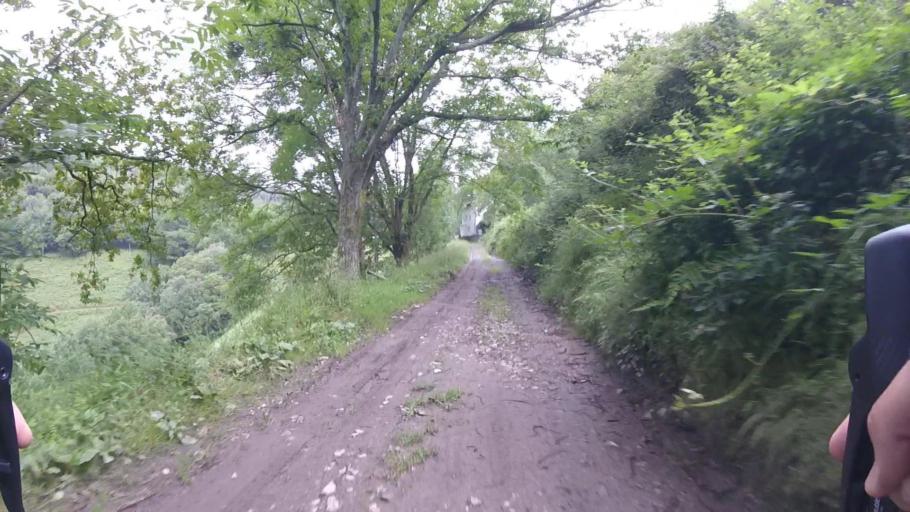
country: ES
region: Basque Country
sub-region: Provincia de Guipuzcoa
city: Errenteria
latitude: 43.2663
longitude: -1.8508
